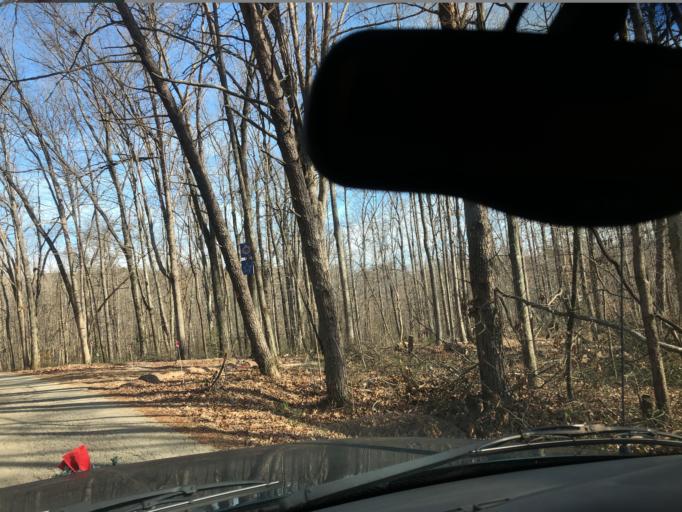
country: US
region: Tennessee
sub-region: Putnam County
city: Monterey
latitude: 35.9927
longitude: -85.2789
